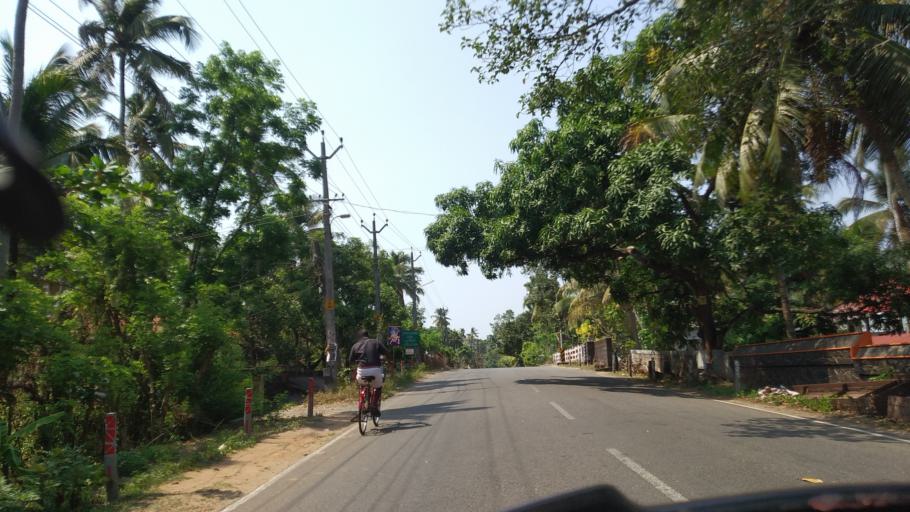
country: IN
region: Kerala
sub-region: Thrissur District
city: Kodungallur
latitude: 10.2257
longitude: 76.1562
